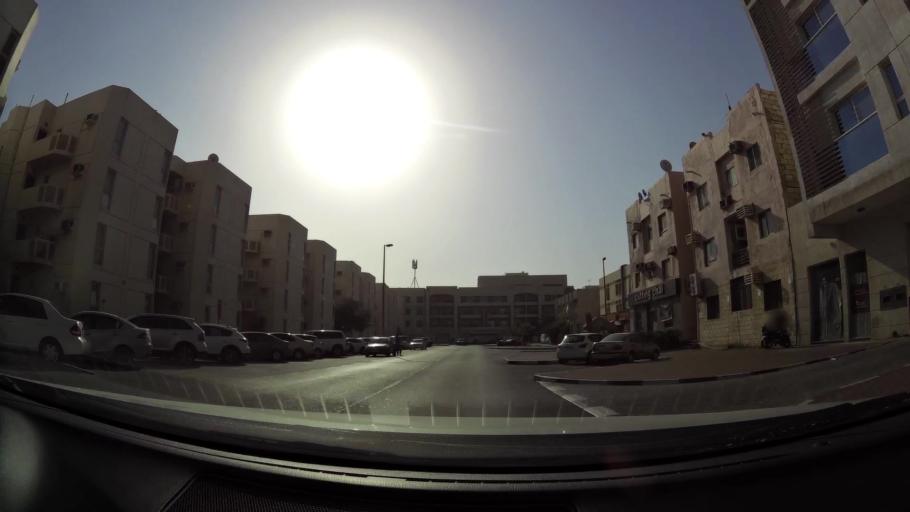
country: AE
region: Ash Shariqah
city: Sharjah
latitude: 25.2409
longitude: 55.2991
